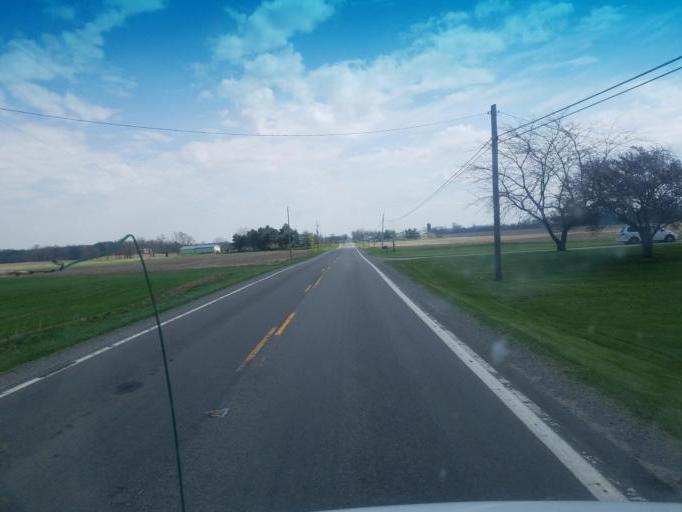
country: US
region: Ohio
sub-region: Hardin County
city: Kenton
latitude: 40.6180
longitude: -83.6647
